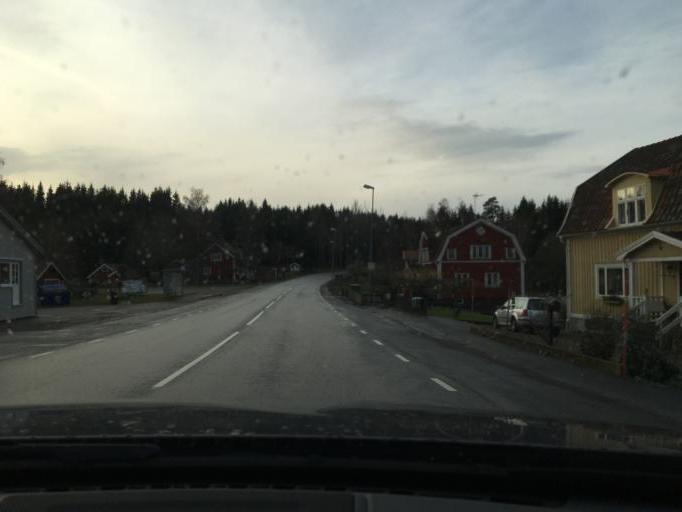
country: SE
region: Joenkoeping
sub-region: Jonkopings Kommun
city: Graenna
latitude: 57.9508
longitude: 14.4146
